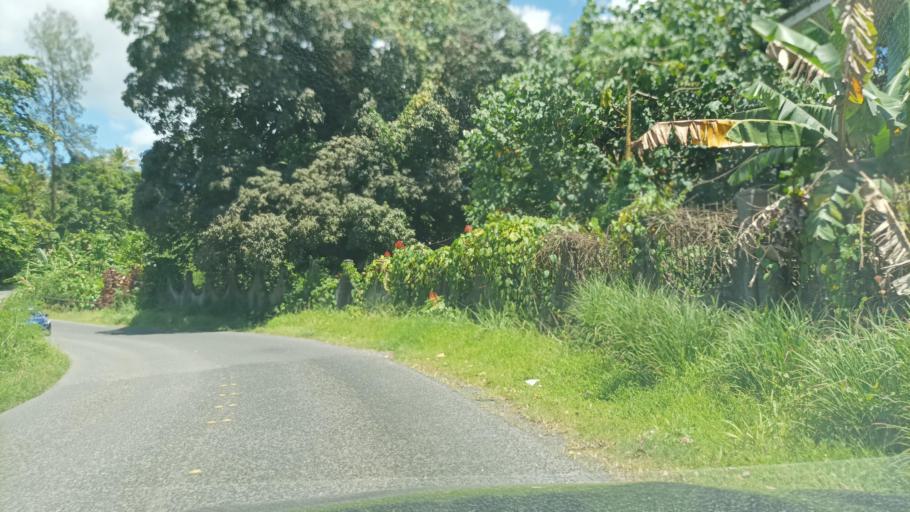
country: FM
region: Pohnpei
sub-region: Kolonia Municipality
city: Kolonia
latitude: 6.9552
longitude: 158.2169
